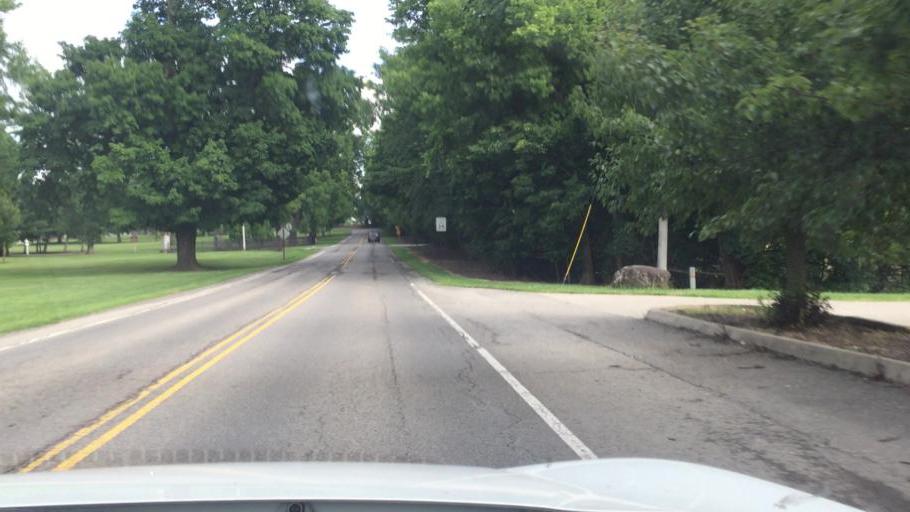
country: US
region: Ohio
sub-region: Champaign County
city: Urbana
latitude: 40.1030
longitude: -83.7371
